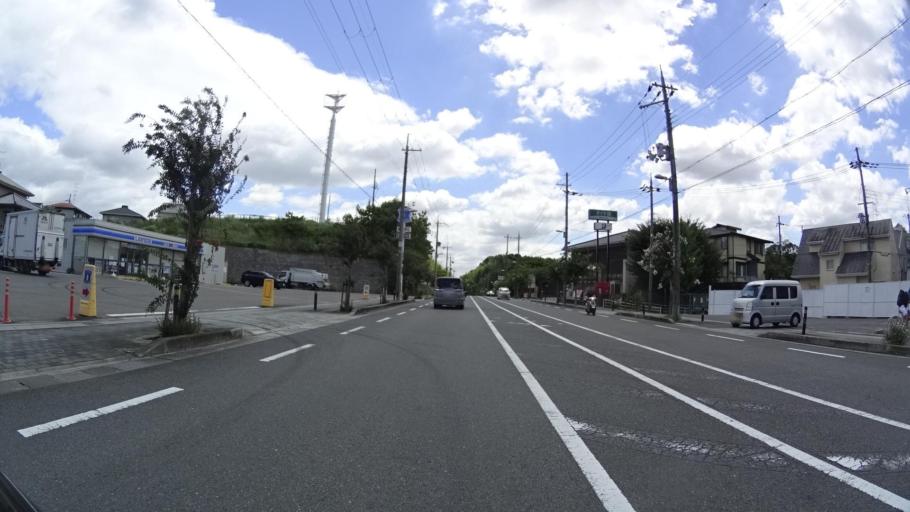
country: JP
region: Kyoto
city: Yawata
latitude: 34.8538
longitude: 135.7022
